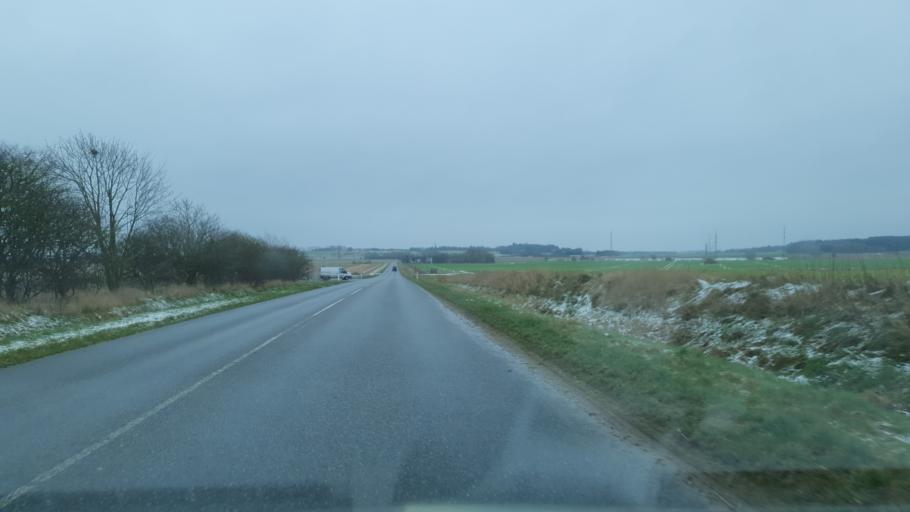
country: DK
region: North Denmark
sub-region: Jammerbugt Kommune
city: Brovst
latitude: 57.1234
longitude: 9.4905
